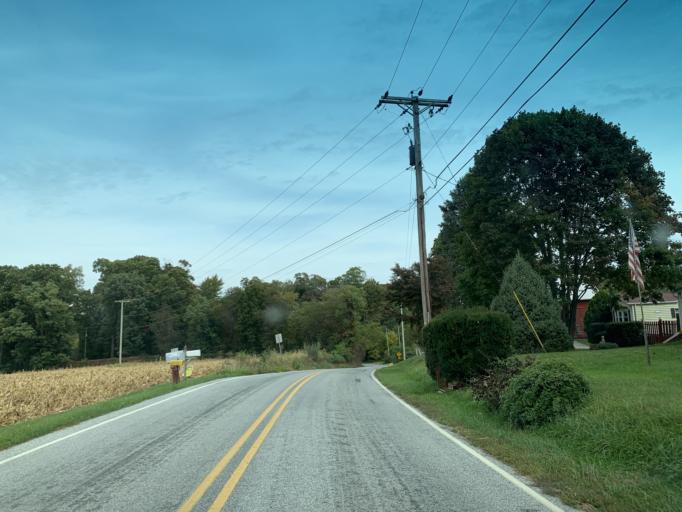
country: US
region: Pennsylvania
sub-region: York County
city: Stewartstown
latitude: 39.8128
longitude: -76.5236
